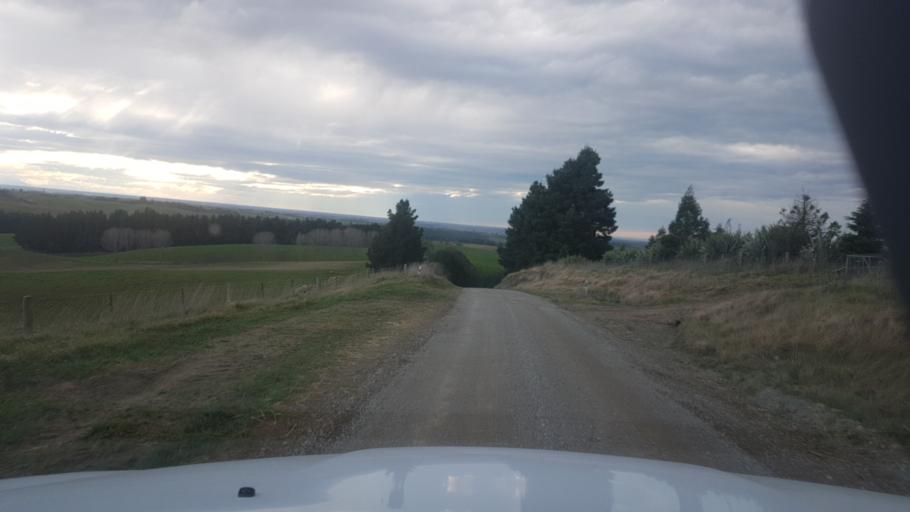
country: NZ
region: Canterbury
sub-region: Timaru District
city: Pleasant Point
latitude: -44.3442
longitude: 171.1379
